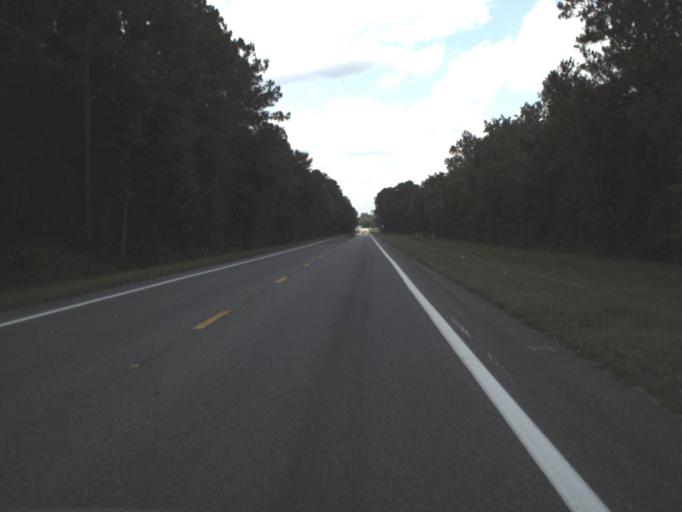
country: US
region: Florida
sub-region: Union County
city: Lake Butler
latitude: 30.0876
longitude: -82.2160
